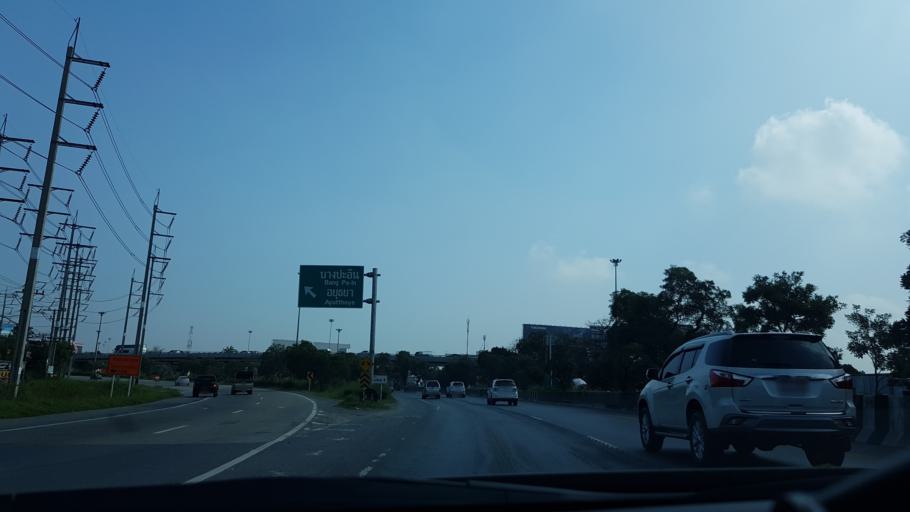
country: TH
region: Phra Nakhon Si Ayutthaya
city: Bang Pa-in
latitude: 14.1711
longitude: 100.6160
